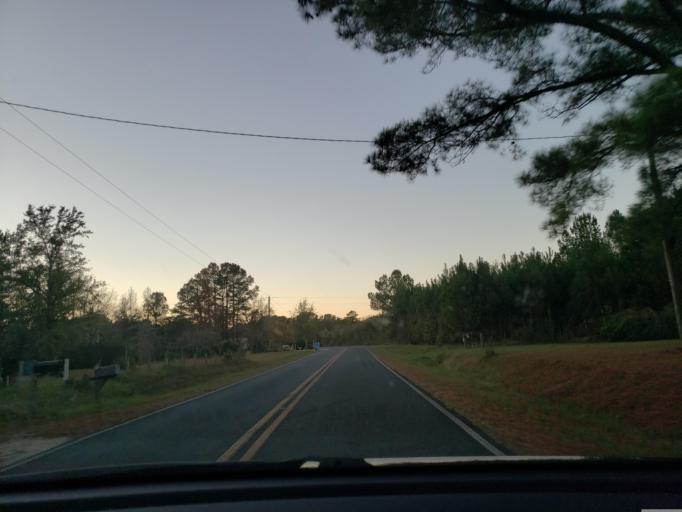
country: US
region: North Carolina
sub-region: Onslow County
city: Richlands
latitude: 34.7477
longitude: -77.6481
